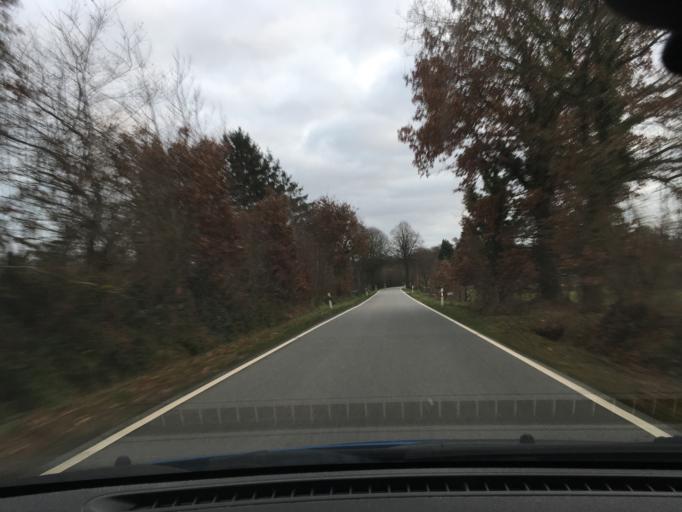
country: DE
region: Schleswig-Holstein
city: Agethorst
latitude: 54.0129
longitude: 9.4323
